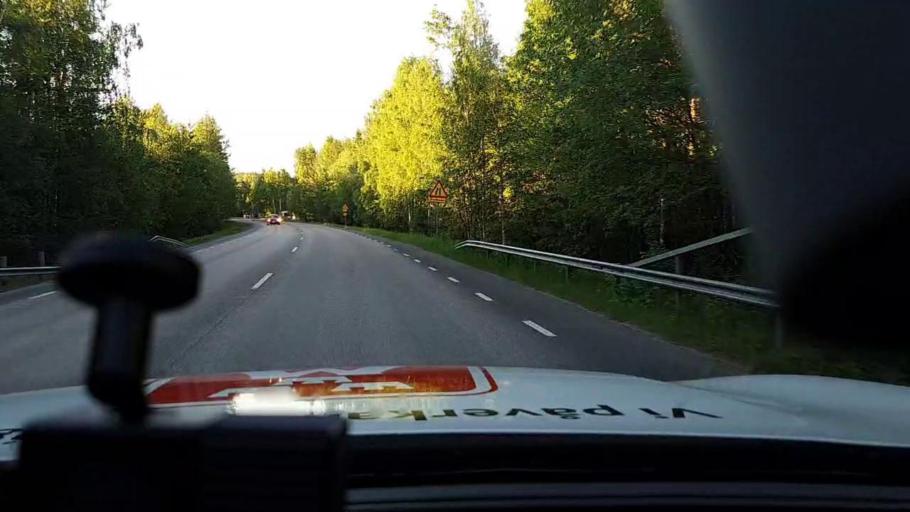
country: SE
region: Norrbotten
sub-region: Lulea Kommun
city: Lulea
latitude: 65.6166
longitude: 22.2000
